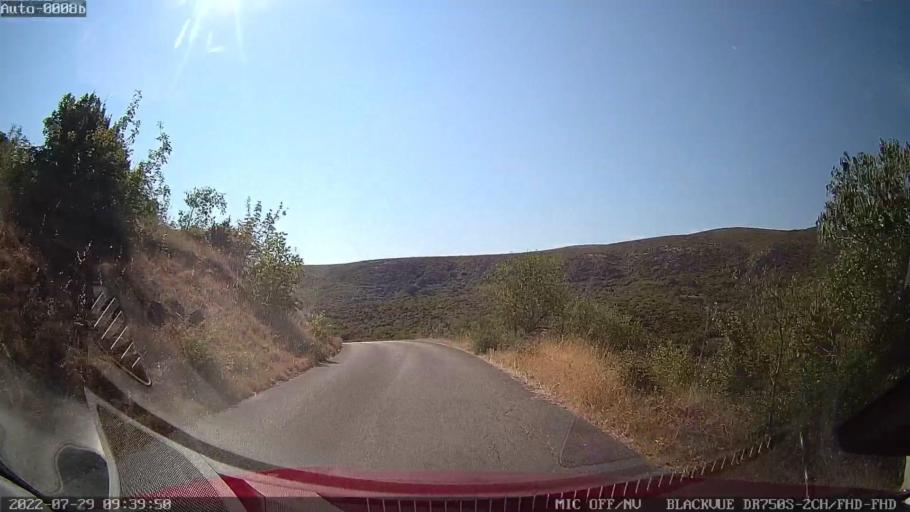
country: HR
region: Zadarska
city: Obrovac
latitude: 44.1940
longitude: 15.7591
